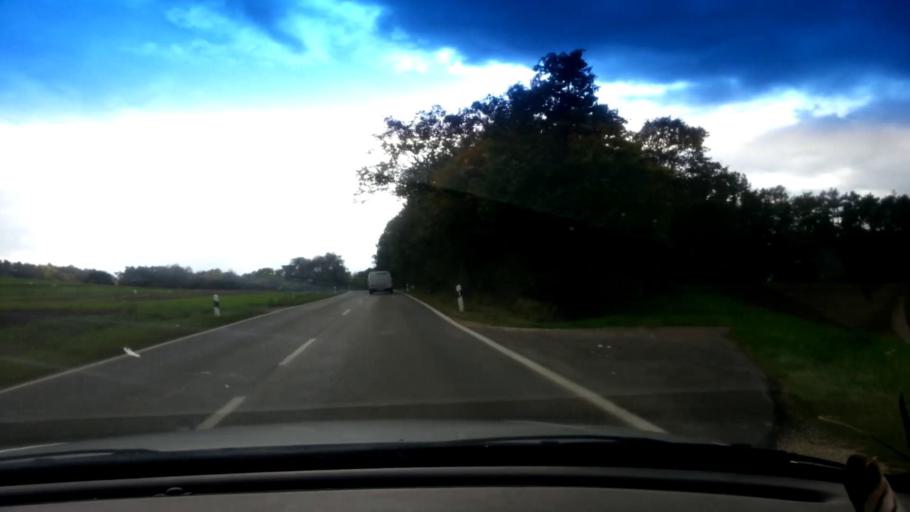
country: DE
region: Bavaria
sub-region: Upper Franconia
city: Zapfendorf
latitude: 49.9979
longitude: 10.9656
